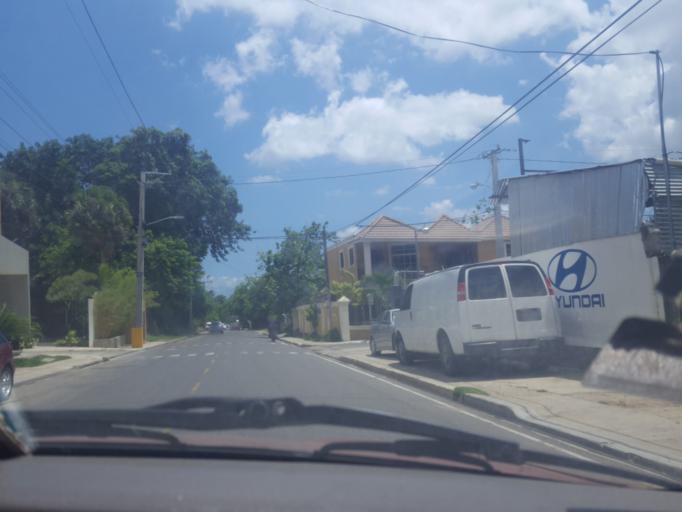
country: DO
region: Santiago
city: Tamboril
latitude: 19.4815
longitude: -70.6576
